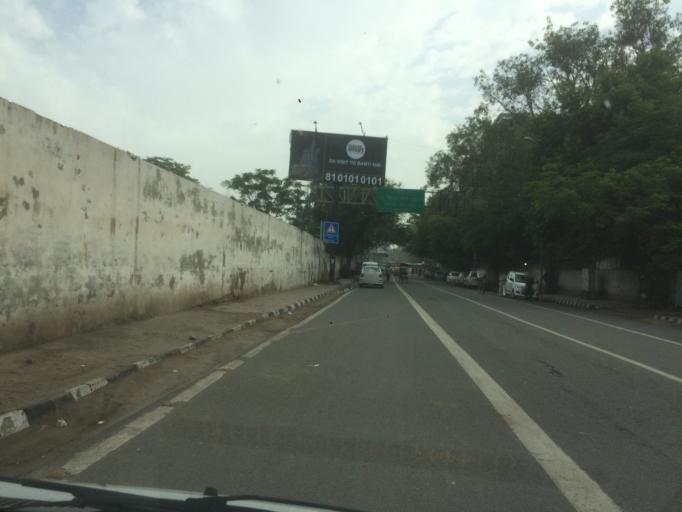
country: IN
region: NCT
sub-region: New Delhi
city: New Delhi
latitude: 28.6405
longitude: 77.2234
